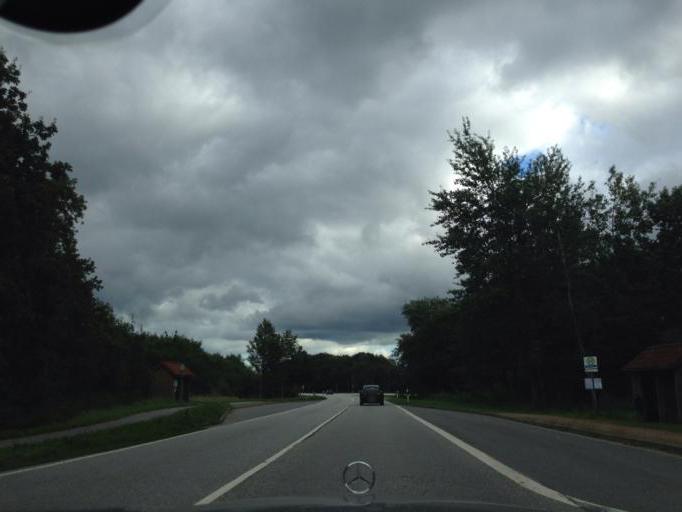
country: DE
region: Schleswig-Holstein
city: Stadum
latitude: 54.7452
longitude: 9.0301
